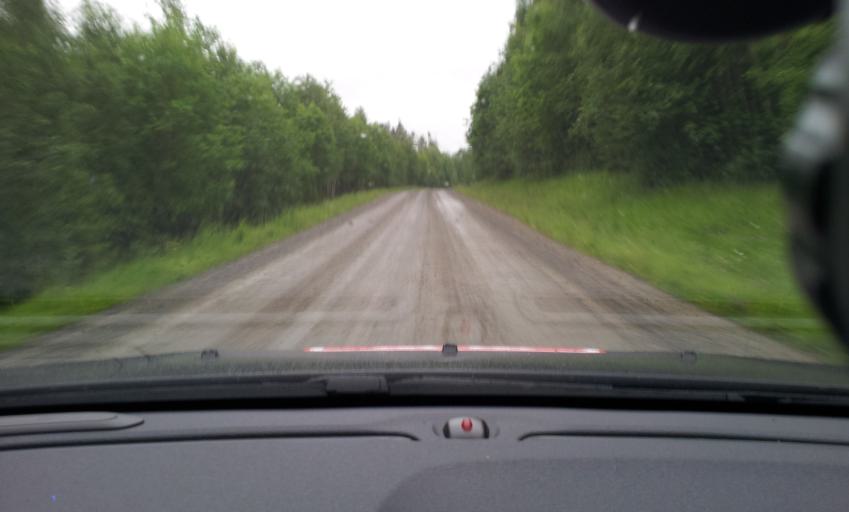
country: SE
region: Jaemtland
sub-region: Ragunda Kommun
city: Hammarstrand
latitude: 63.1417
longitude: 16.0786
